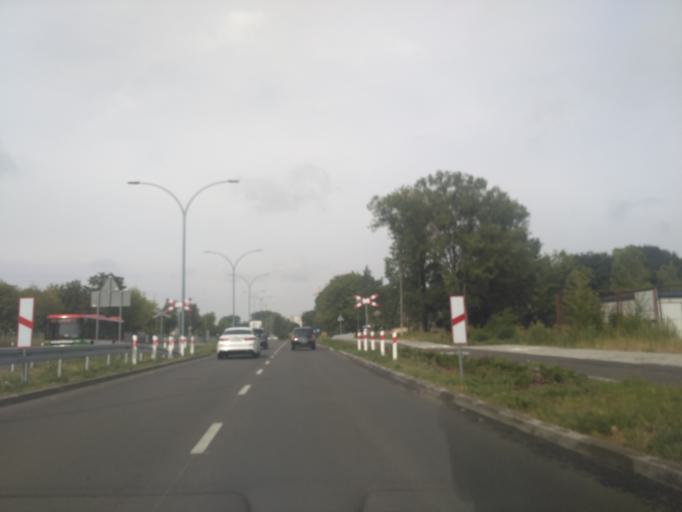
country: PL
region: Lublin Voivodeship
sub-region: Powiat lubelski
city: Lublin
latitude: 51.2232
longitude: 22.5705
